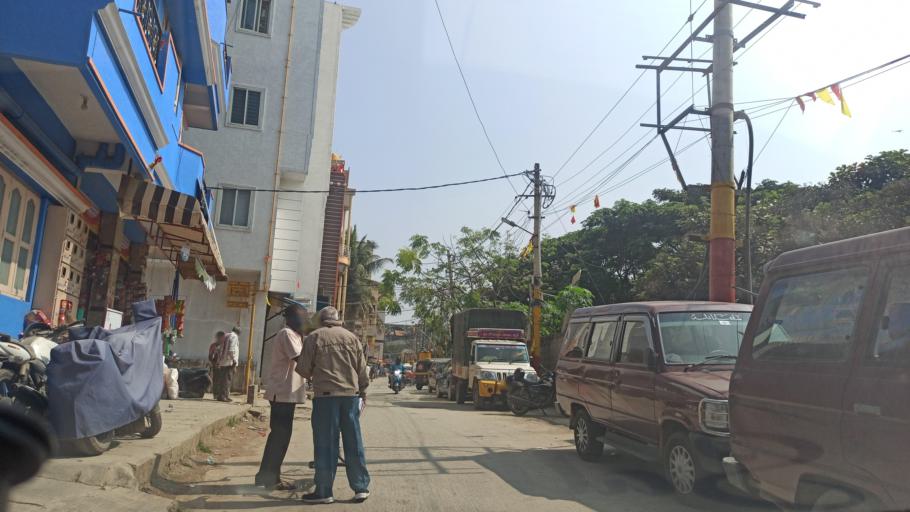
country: IN
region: Karnataka
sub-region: Bangalore Urban
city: Bangalore
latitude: 12.9574
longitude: 77.6961
